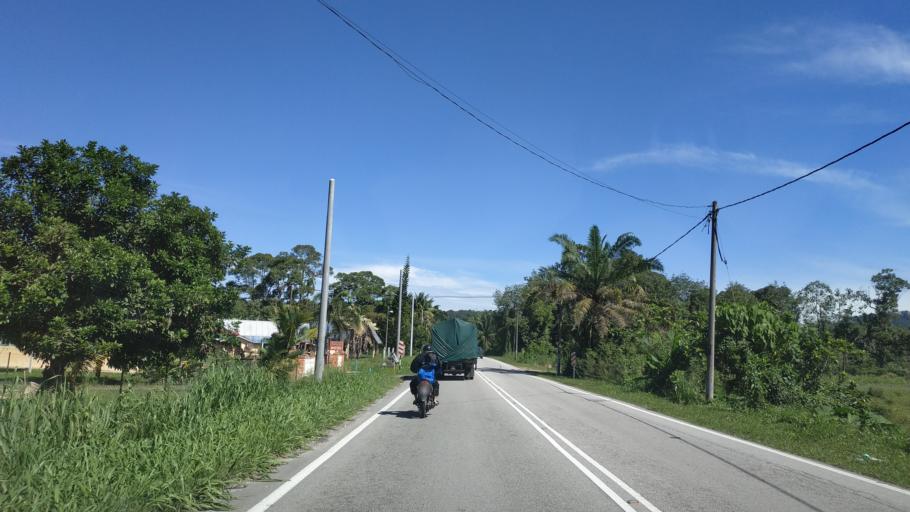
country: MY
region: Kedah
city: Kulim
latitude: 5.3123
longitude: 100.5402
